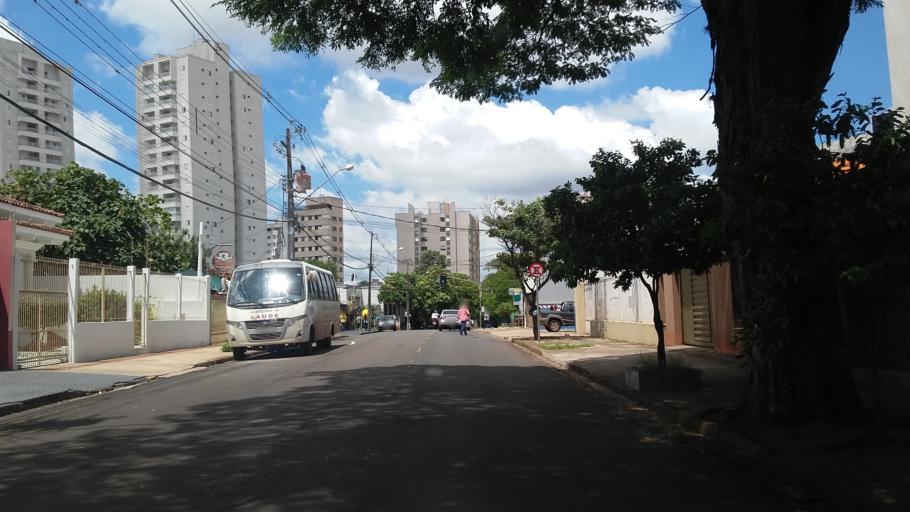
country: BR
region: Parana
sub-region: Londrina
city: Londrina
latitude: -23.3046
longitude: -51.1676
